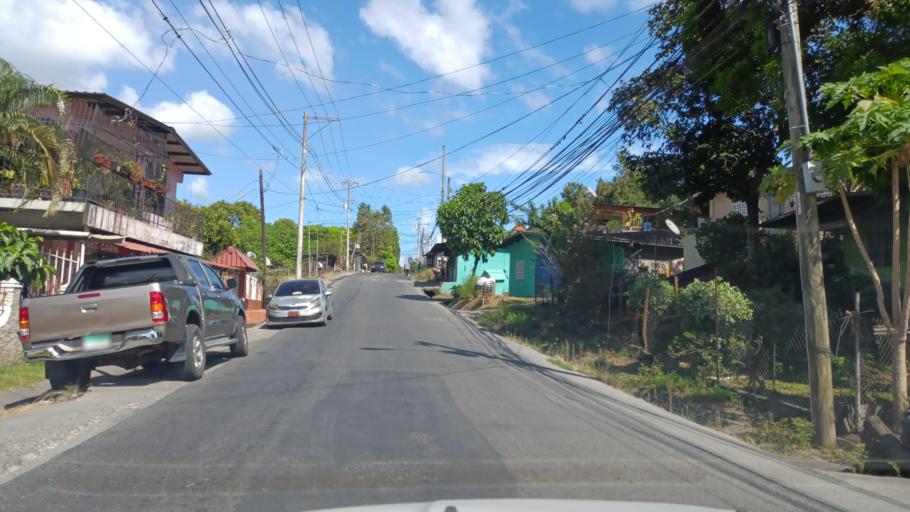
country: PA
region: Panama
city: Tocumen
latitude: 9.1003
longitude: -79.3704
